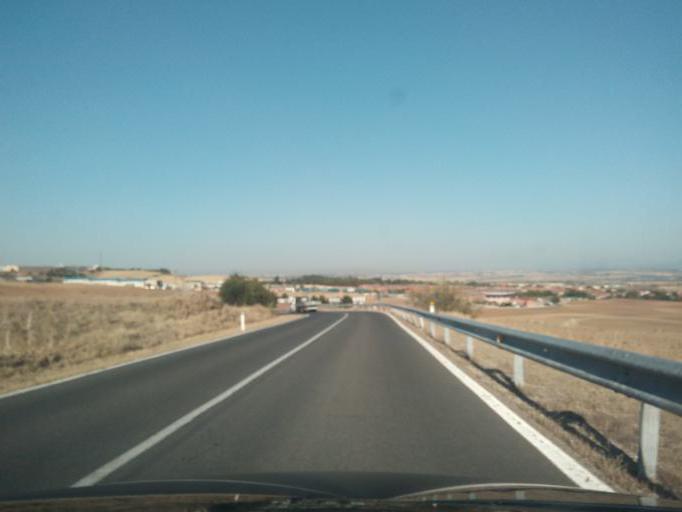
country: ES
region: Madrid
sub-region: Provincia de Madrid
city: Cobena
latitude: 40.5649
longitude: -3.4896
